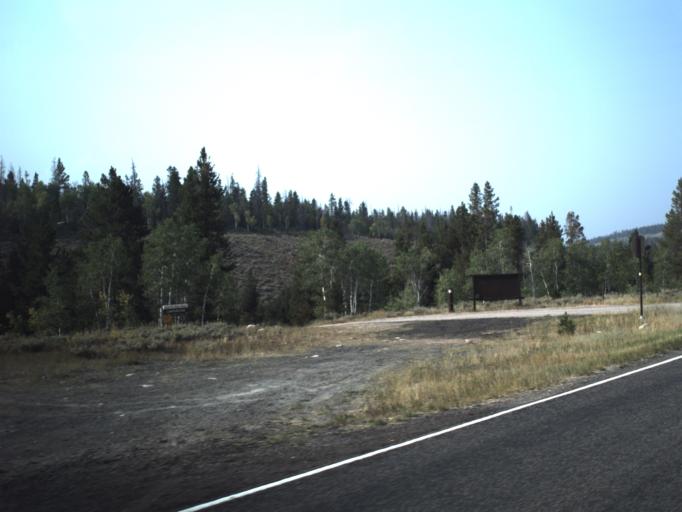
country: US
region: Wyoming
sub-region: Uinta County
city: Evanston
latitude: 40.9115
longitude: -110.8293
